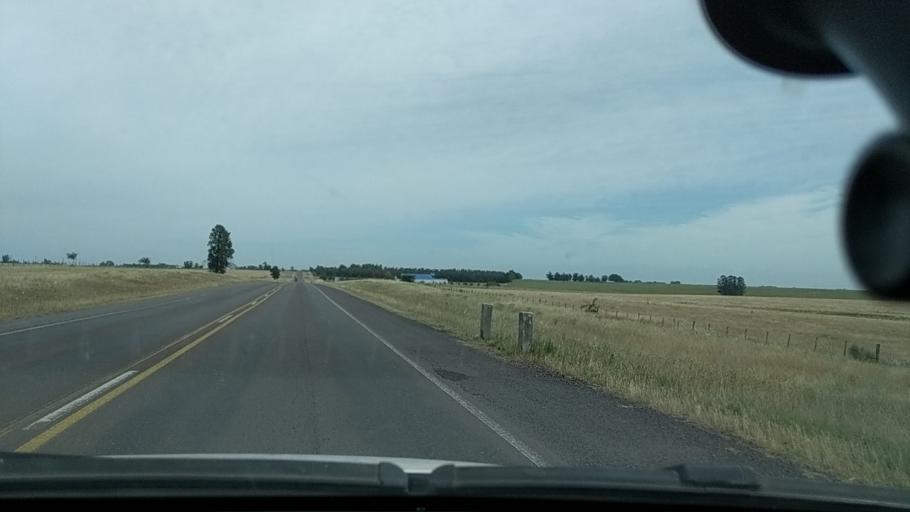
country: UY
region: Durazno
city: Durazno
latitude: -33.4599
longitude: -56.4642
